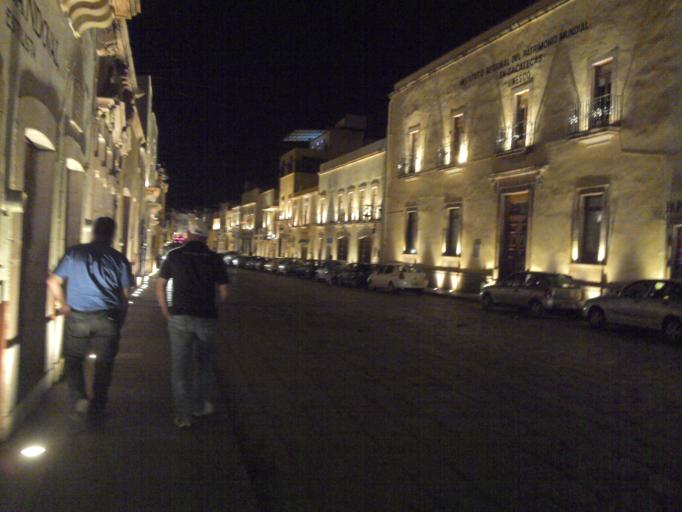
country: MX
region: Zacatecas
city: Zacatecas
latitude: 22.7798
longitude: -102.5714
